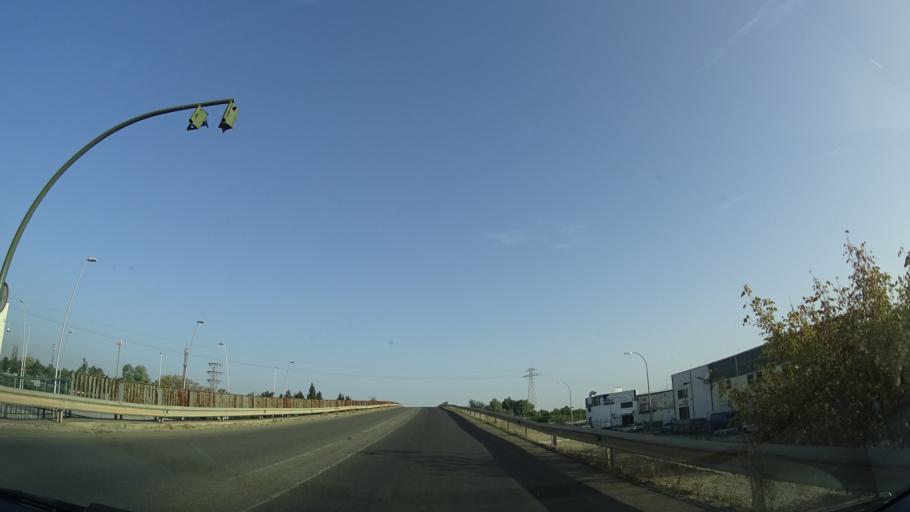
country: ES
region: Andalusia
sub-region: Provincia de Sevilla
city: La Algaba
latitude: 37.4329
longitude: -5.9799
